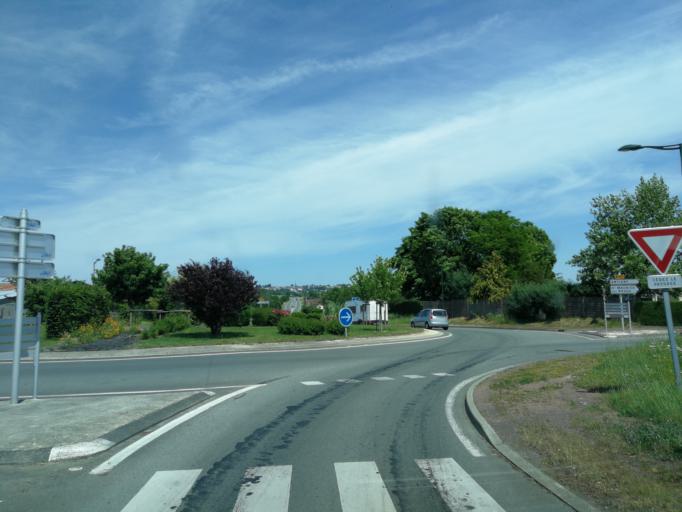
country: FR
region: Pays de la Loire
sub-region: Departement de la Vendee
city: Antigny
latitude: 46.6261
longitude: -0.7724
